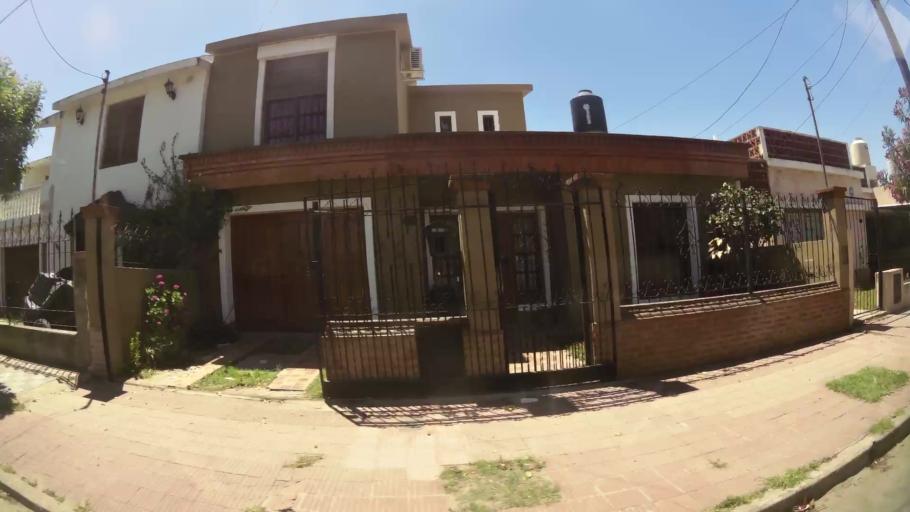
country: AR
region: Cordoba
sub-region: Departamento de Capital
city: Cordoba
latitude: -31.4317
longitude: -64.1272
